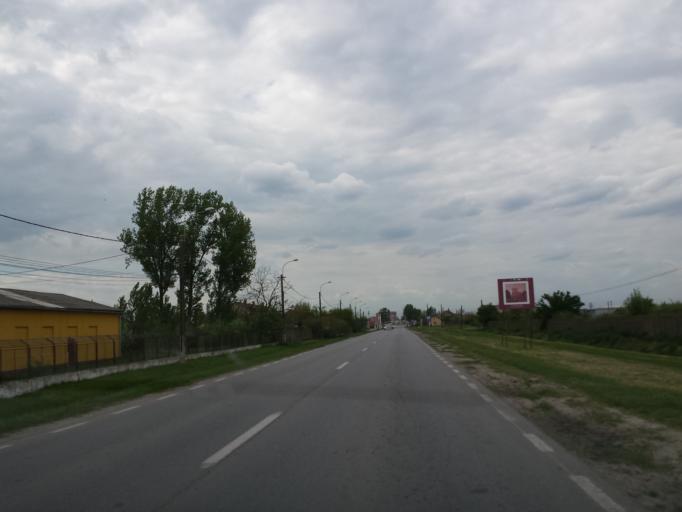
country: RO
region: Timis
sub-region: Comuna Sanpetru Mare
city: Sanpetru Mare
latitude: 46.0527
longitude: 20.6458
